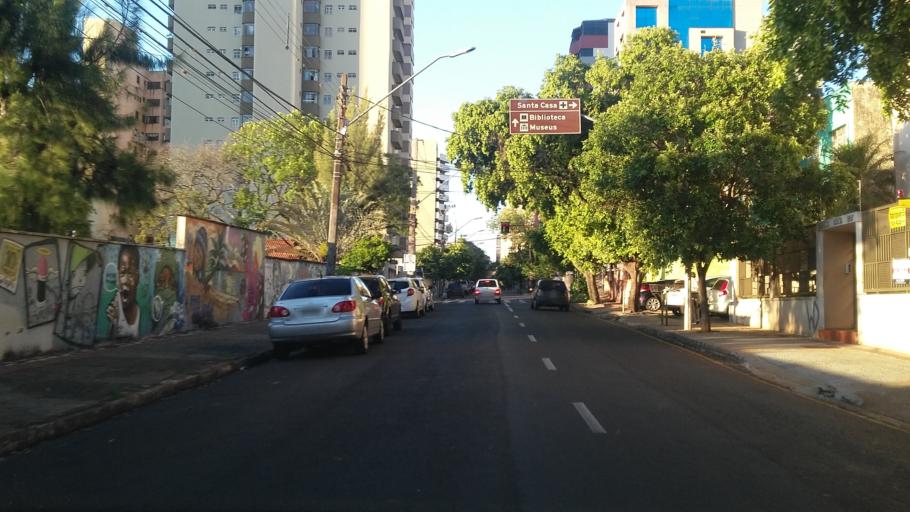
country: BR
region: Parana
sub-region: Londrina
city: Londrina
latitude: -23.3182
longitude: -51.1589
